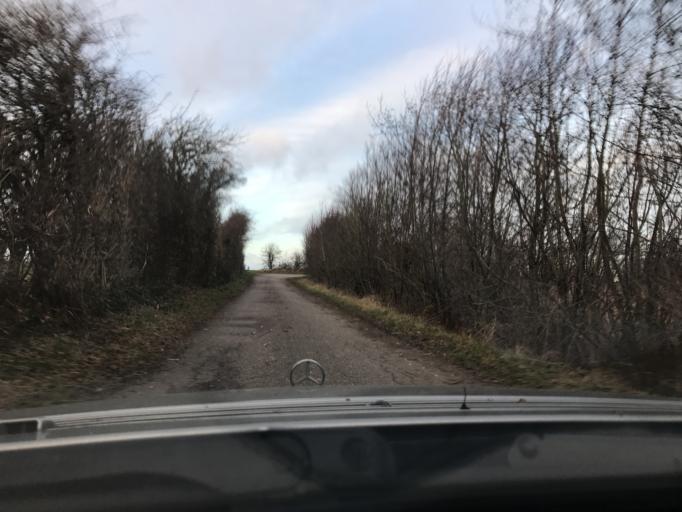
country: DK
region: South Denmark
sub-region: Sonderborg Kommune
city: Nordborg
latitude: 55.0448
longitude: 9.6539
